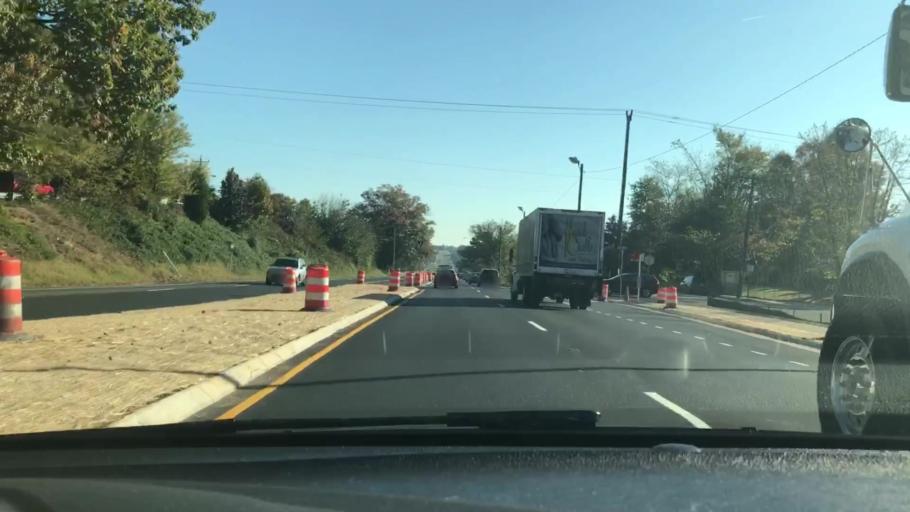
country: US
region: Virginia
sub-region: Fairfax County
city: Jefferson
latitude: 38.8674
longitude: -77.1878
